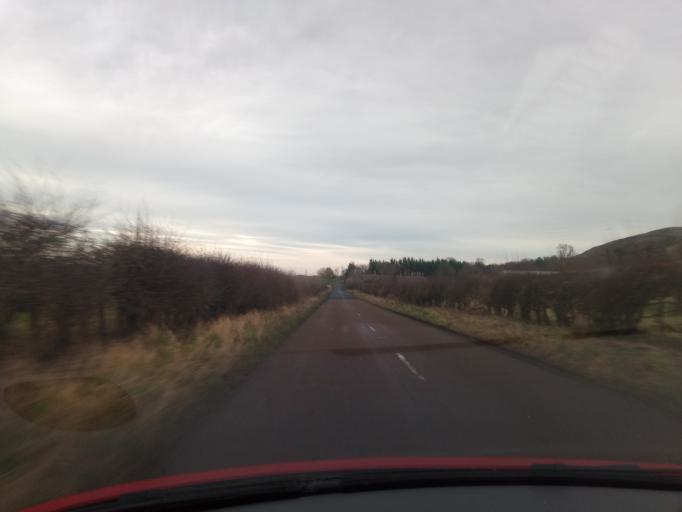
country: GB
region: England
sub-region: Northumberland
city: Kirknewton
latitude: 55.5617
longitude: -2.0746
